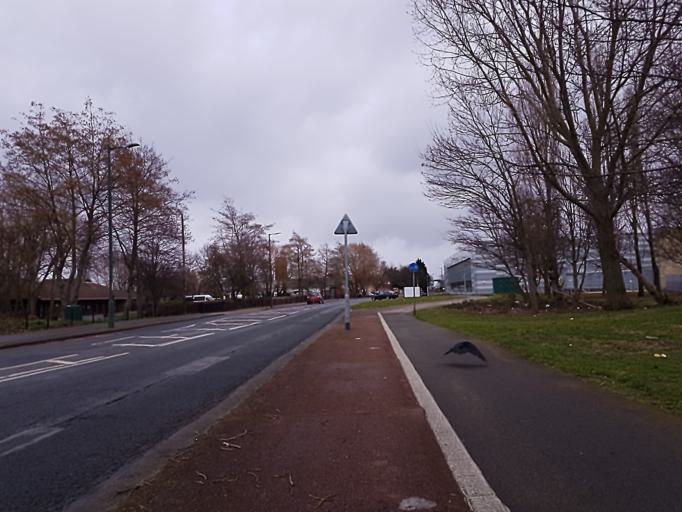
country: GB
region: England
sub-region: North East Lincolnshire
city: Grimbsy
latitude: 53.5699
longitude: -0.1153
